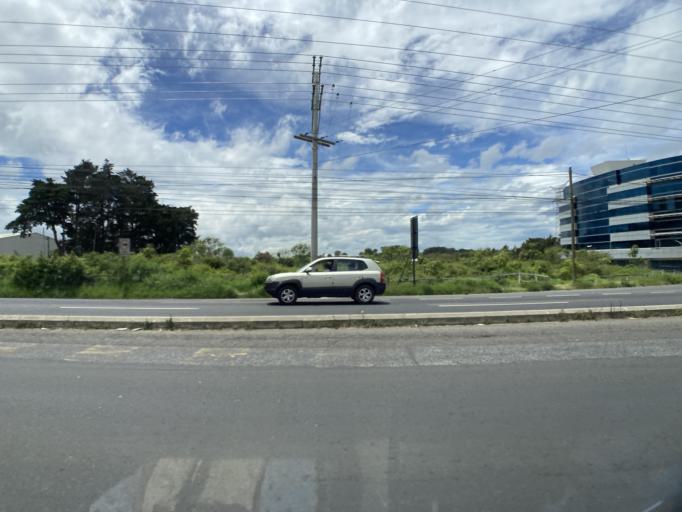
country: GT
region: Guatemala
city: Villa Canales
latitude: 14.4990
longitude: -90.4818
